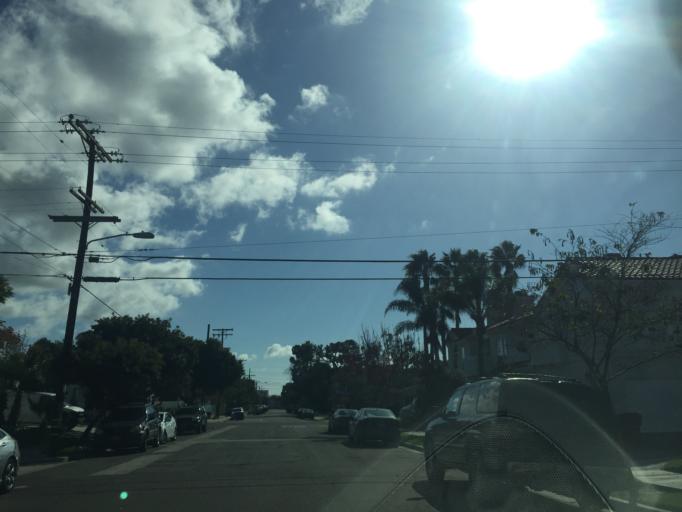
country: US
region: California
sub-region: San Diego County
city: La Jolla
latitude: 32.7940
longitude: -117.2430
